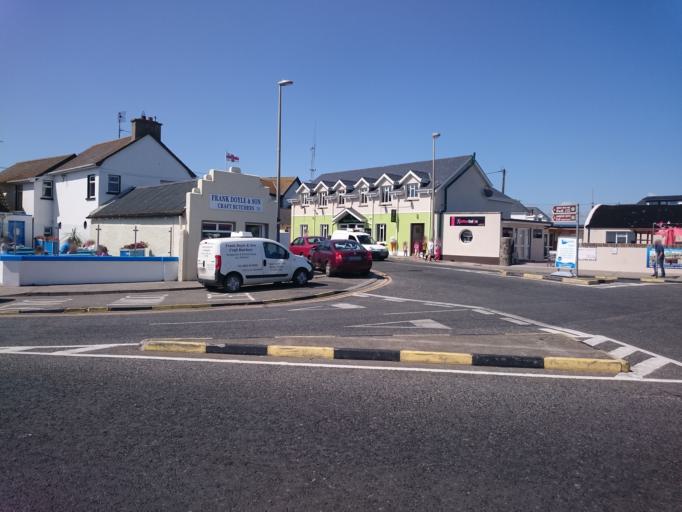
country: IE
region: Leinster
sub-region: Loch Garman
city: Loch Garman
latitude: 52.1727
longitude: -6.5892
